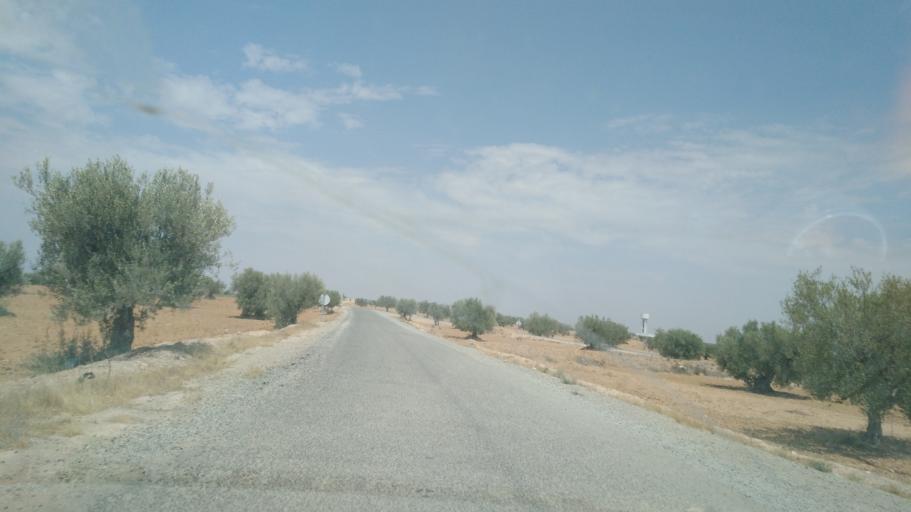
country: TN
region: Safaqis
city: Sfax
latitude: 34.7469
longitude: 10.5612
